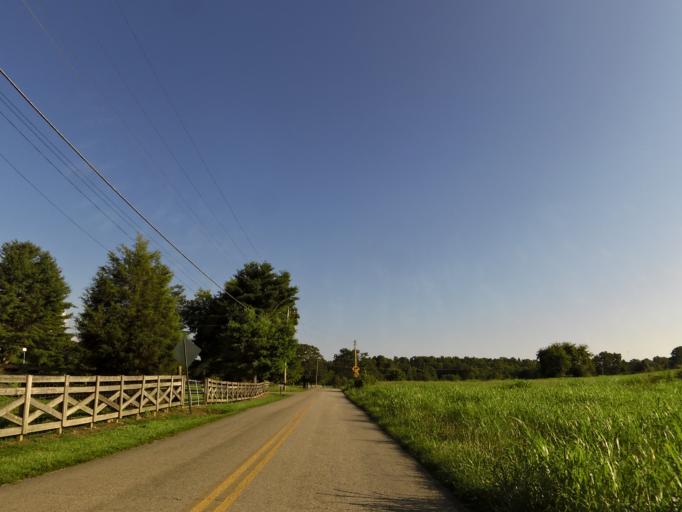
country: US
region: Tennessee
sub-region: Blount County
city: Eagleton Village
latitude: 35.7331
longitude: -83.8974
